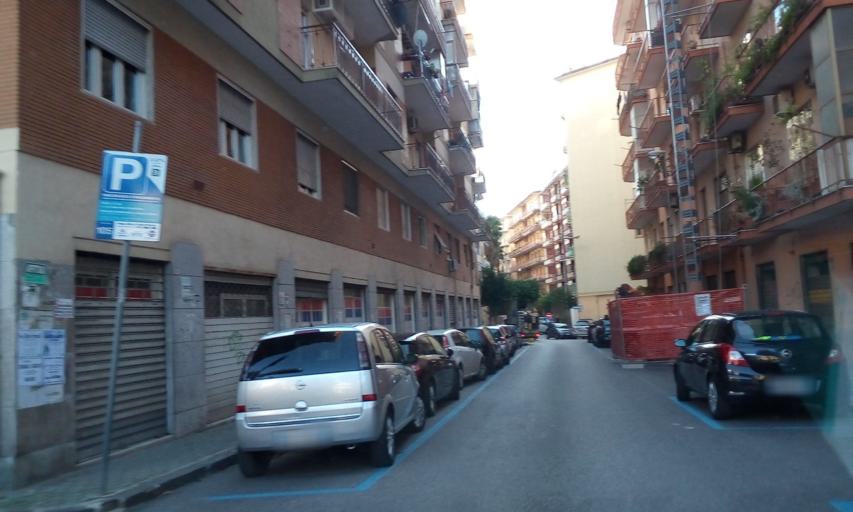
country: IT
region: Campania
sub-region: Provincia di Salerno
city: Salerno
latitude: 40.6795
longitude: 14.7764
